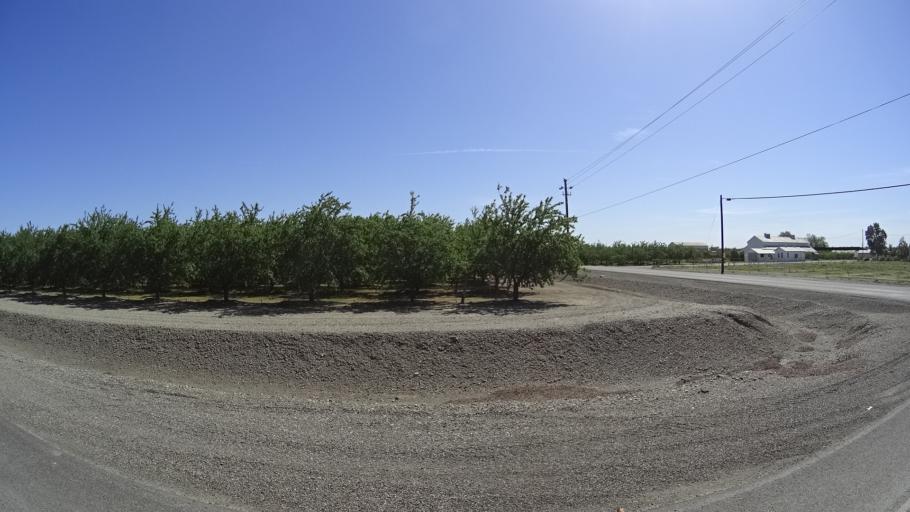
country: US
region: California
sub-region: Glenn County
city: Hamilton City
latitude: 39.7106
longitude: -122.1043
